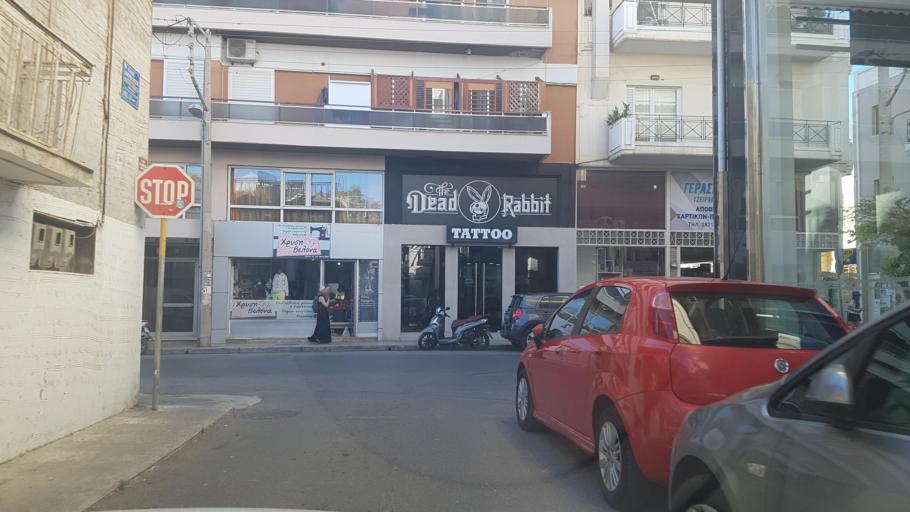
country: GR
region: Crete
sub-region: Nomos Chanias
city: Chania
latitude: 35.5130
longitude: 24.0116
